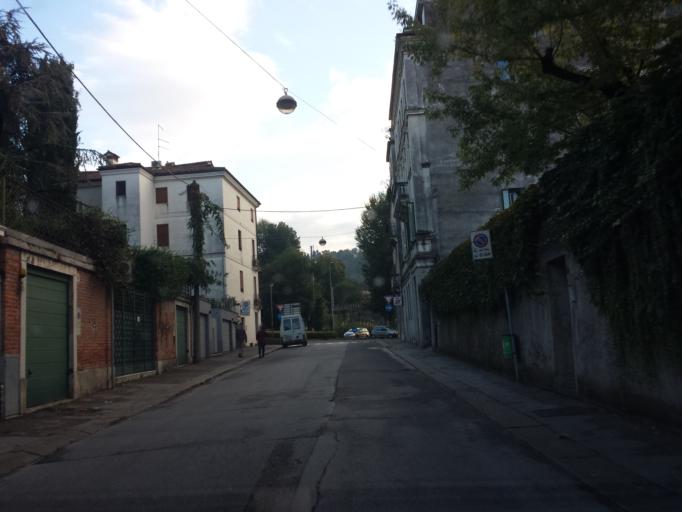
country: IT
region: Veneto
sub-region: Provincia di Vicenza
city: Vicenza
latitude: 45.5420
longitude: 11.5468
